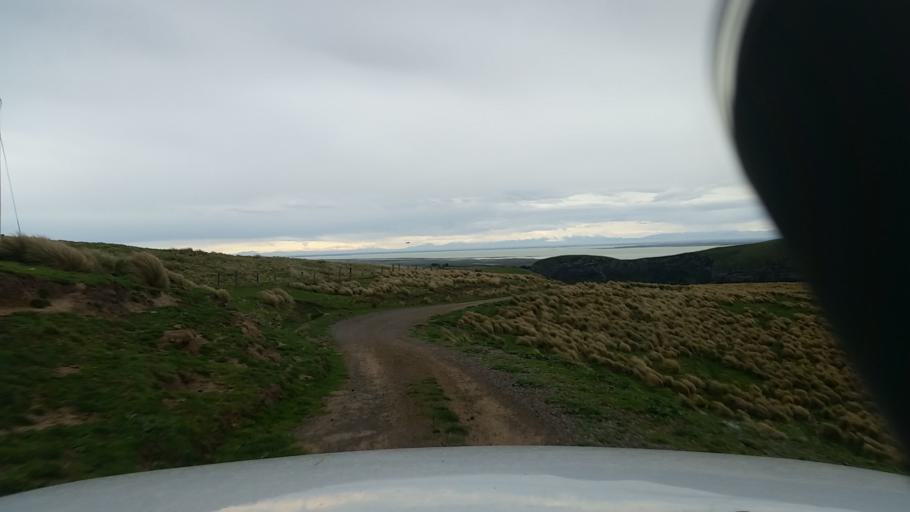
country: NZ
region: Canterbury
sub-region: Selwyn District
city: Lincoln
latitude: -43.8209
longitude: 172.7258
